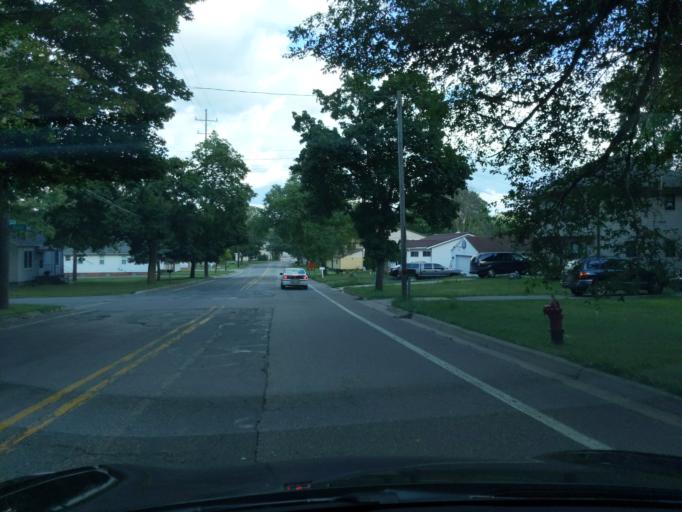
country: US
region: Michigan
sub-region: Jackson County
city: Jackson
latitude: 42.2652
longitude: -84.4146
